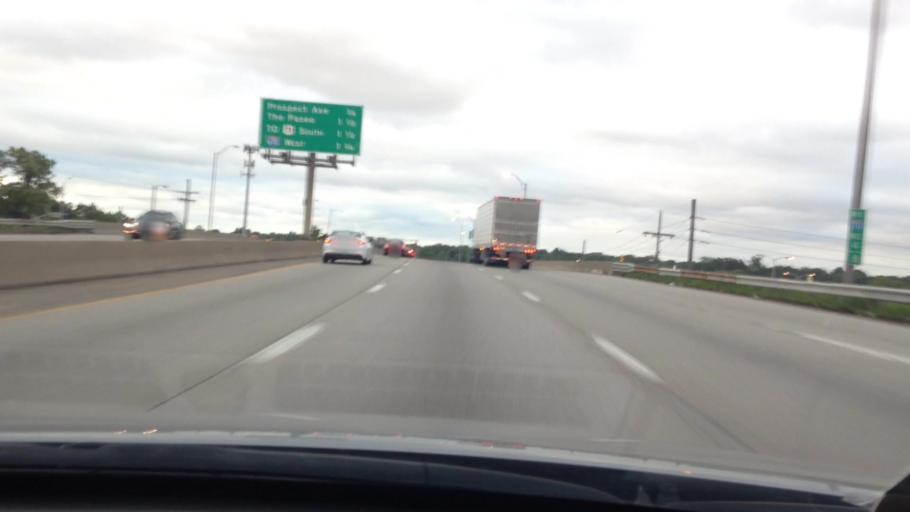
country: US
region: Missouri
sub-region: Jackson County
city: Kansas City
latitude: 39.0897
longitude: -94.5418
